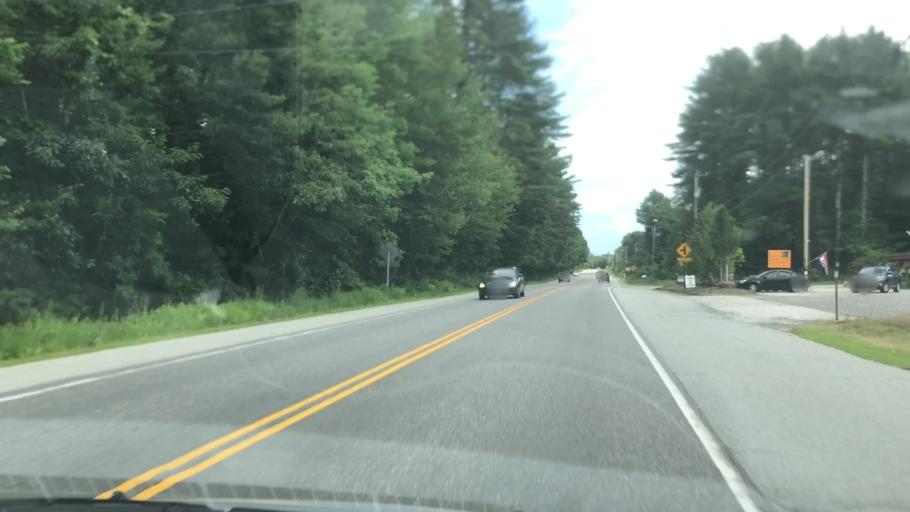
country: US
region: New Hampshire
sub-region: Hillsborough County
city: Mont Vernon
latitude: 42.8985
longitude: -71.5913
